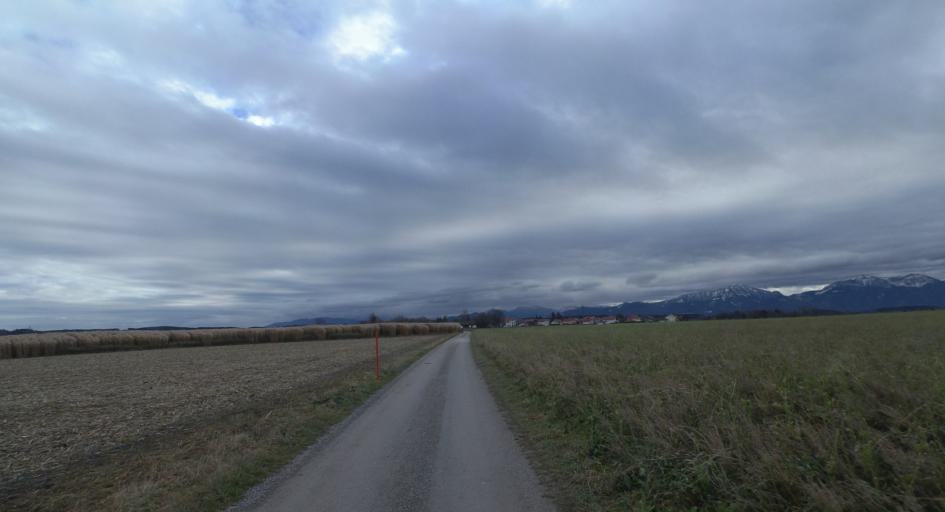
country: DE
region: Bavaria
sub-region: Upper Bavaria
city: Chieming
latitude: 47.9025
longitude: 12.5317
